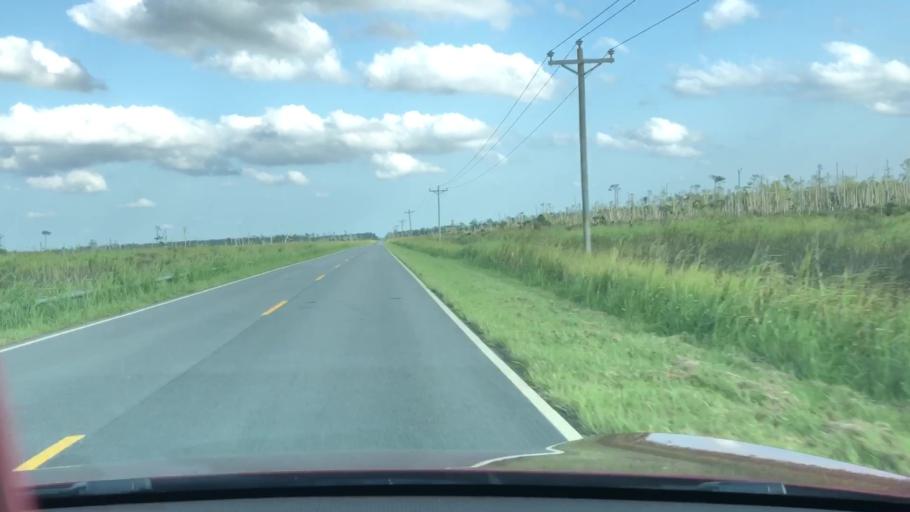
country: US
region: North Carolina
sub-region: Dare County
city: Wanchese
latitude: 35.6295
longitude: -75.8519
